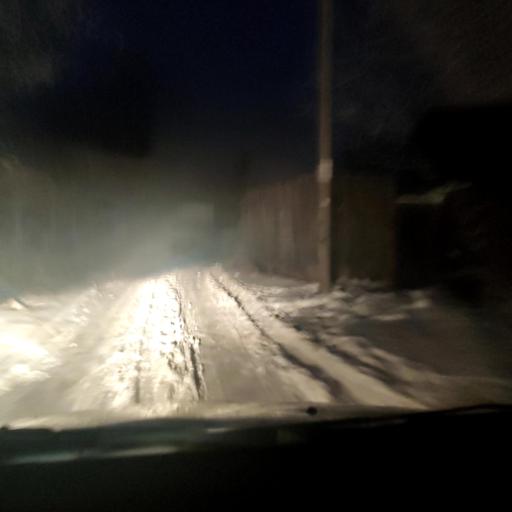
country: RU
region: Bashkortostan
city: Ufa
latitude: 54.7984
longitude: 56.0344
